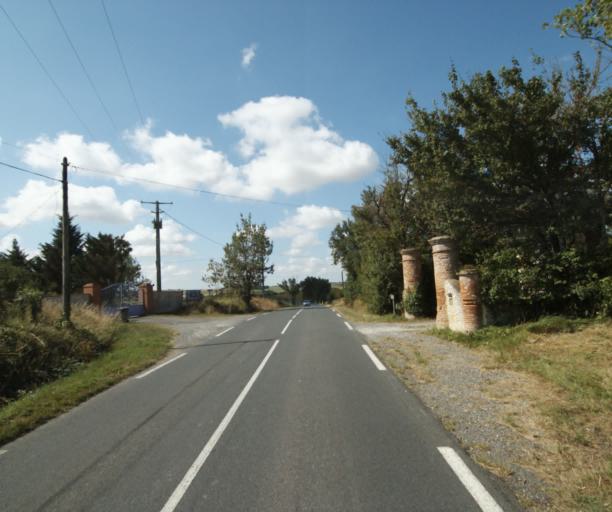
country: FR
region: Midi-Pyrenees
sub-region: Departement de la Haute-Garonne
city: Saint-Felix-Lauragais
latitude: 43.4493
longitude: 1.8134
